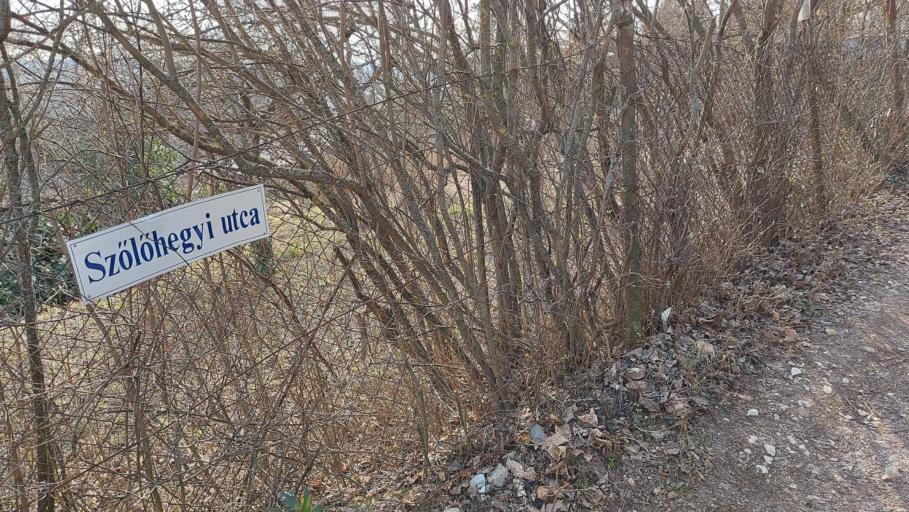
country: HU
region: Pest
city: Budaors
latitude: 47.4739
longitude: 18.9661
